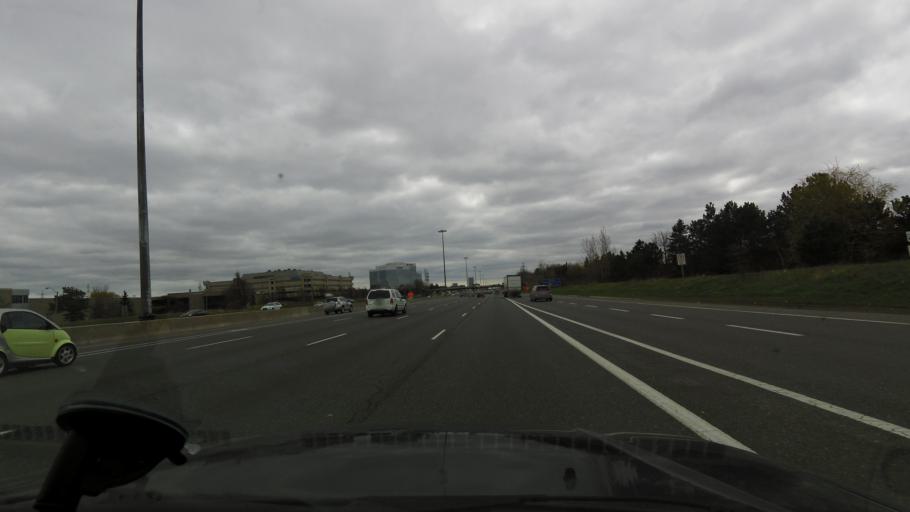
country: CA
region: Ontario
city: Willowdale
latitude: 43.8072
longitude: -79.3465
